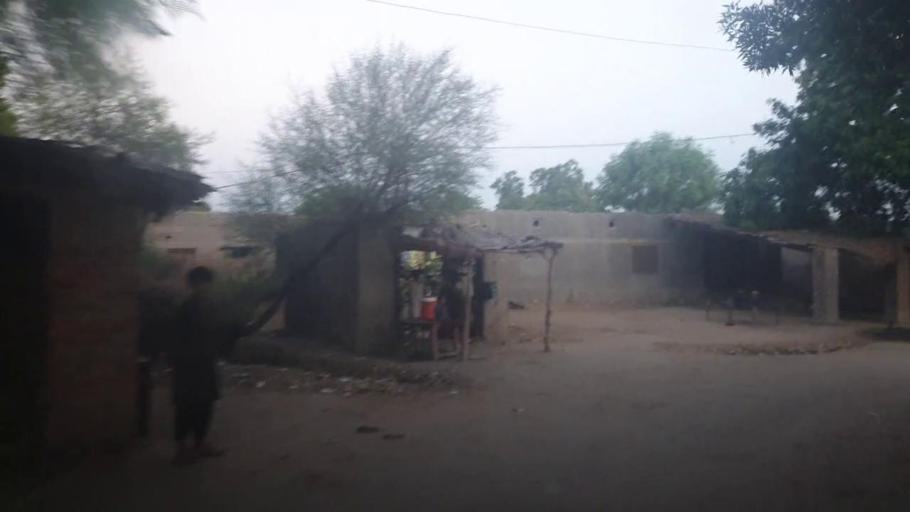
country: PK
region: Sindh
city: Ubauro
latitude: 28.1048
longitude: 69.7818
